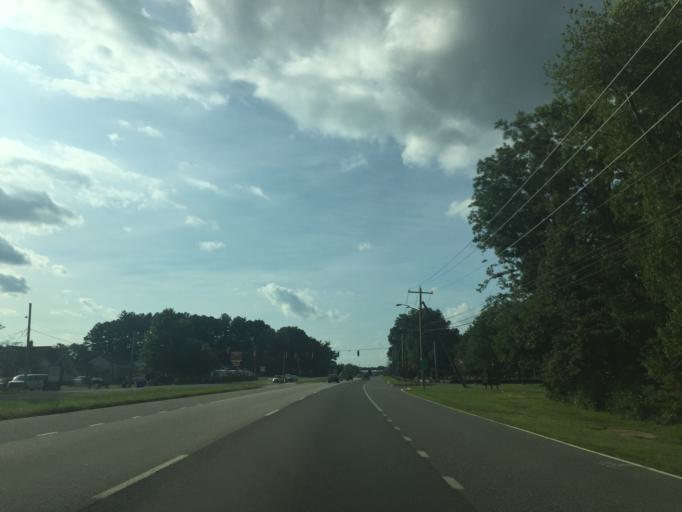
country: US
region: Delaware
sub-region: Kent County
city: Smyrna
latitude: 39.3197
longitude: -75.6185
